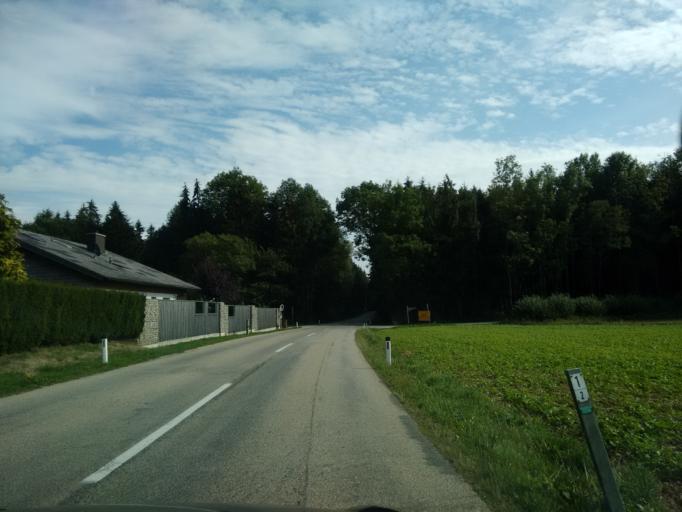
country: AT
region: Upper Austria
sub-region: Wels-Land
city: Thalheim bei Wels
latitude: 48.1373
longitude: 14.0581
